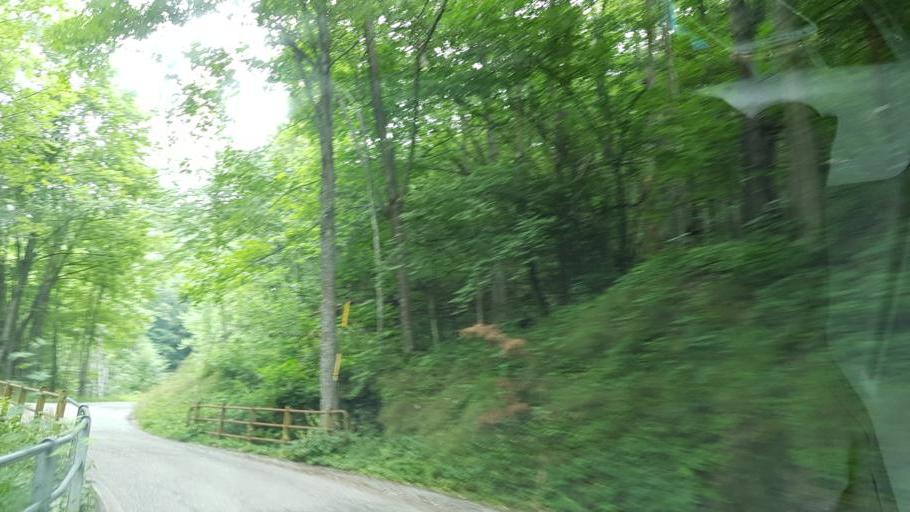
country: IT
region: Piedmont
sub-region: Provincia di Cuneo
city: Stroppo
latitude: 44.5141
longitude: 7.1294
